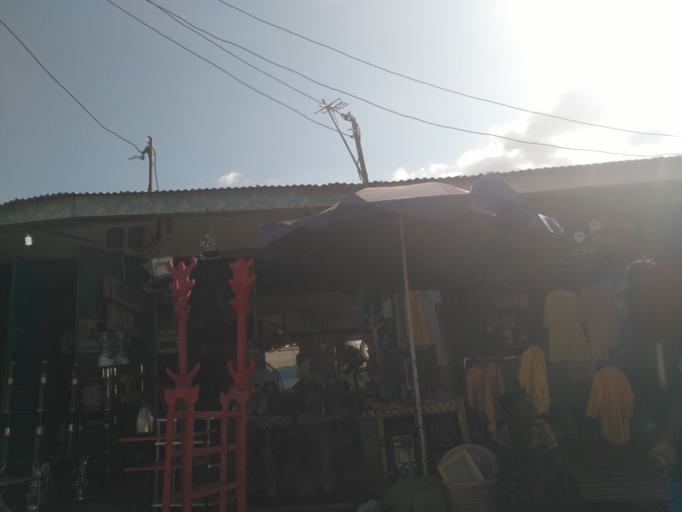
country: TZ
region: Dar es Salaam
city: Dar es Salaam
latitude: -6.8681
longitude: 39.2617
